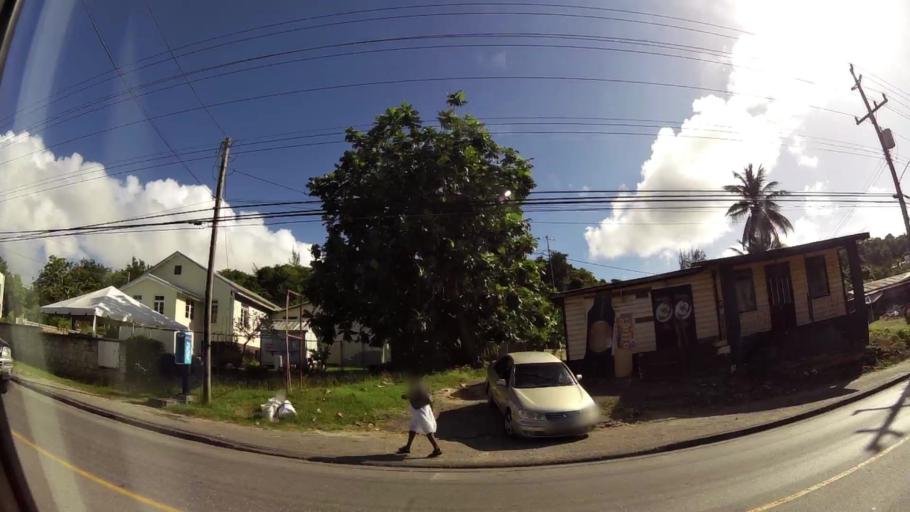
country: BB
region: Saint James
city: Holetown
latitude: 13.2163
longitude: -59.6200
